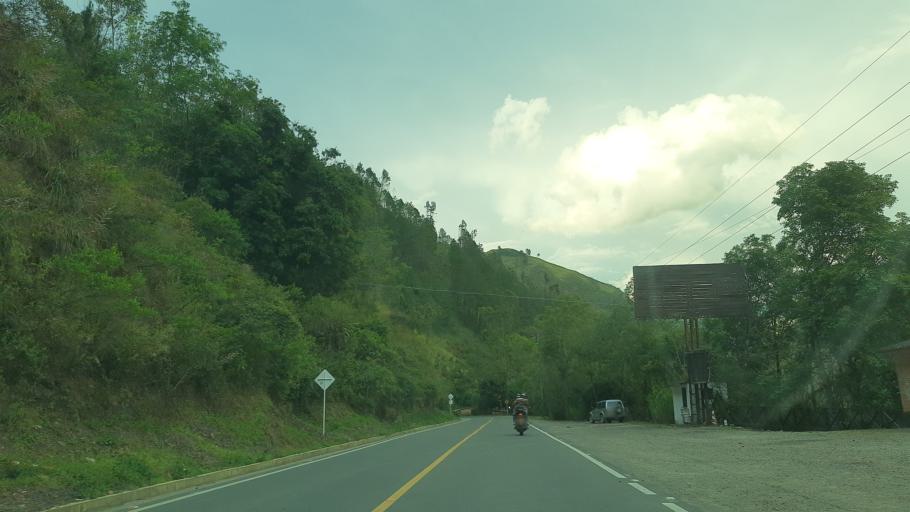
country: CO
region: Boyaca
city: Somondoco
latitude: 5.0127
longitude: -73.3940
